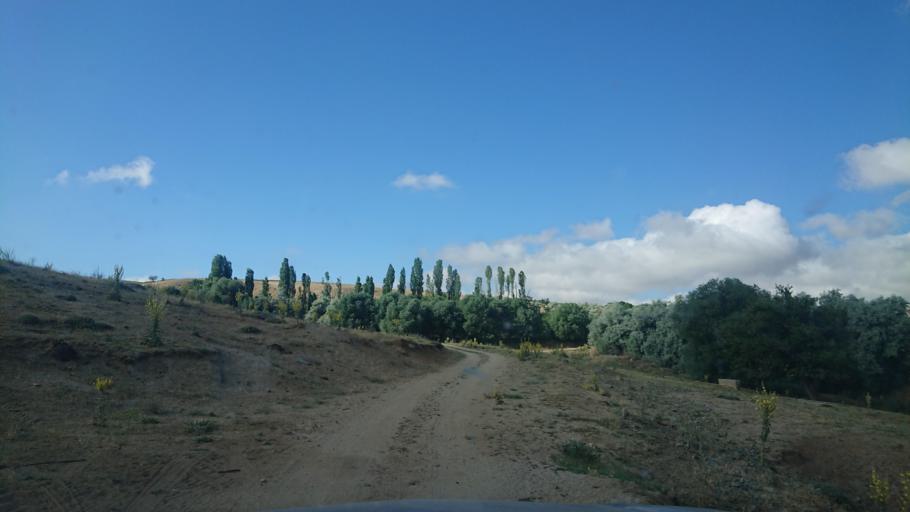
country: TR
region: Aksaray
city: Agacoren
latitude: 38.8532
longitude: 33.9357
